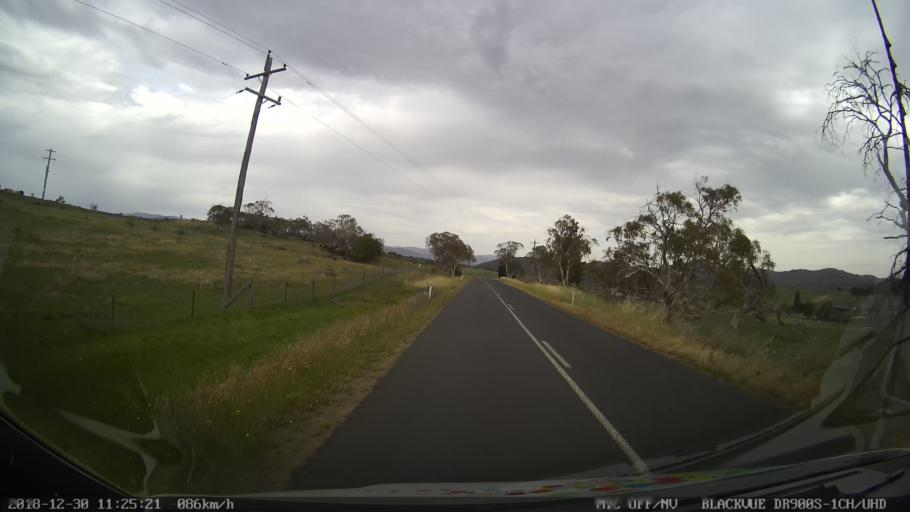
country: AU
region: New South Wales
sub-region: Snowy River
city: Jindabyne
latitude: -36.4724
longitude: 148.6479
